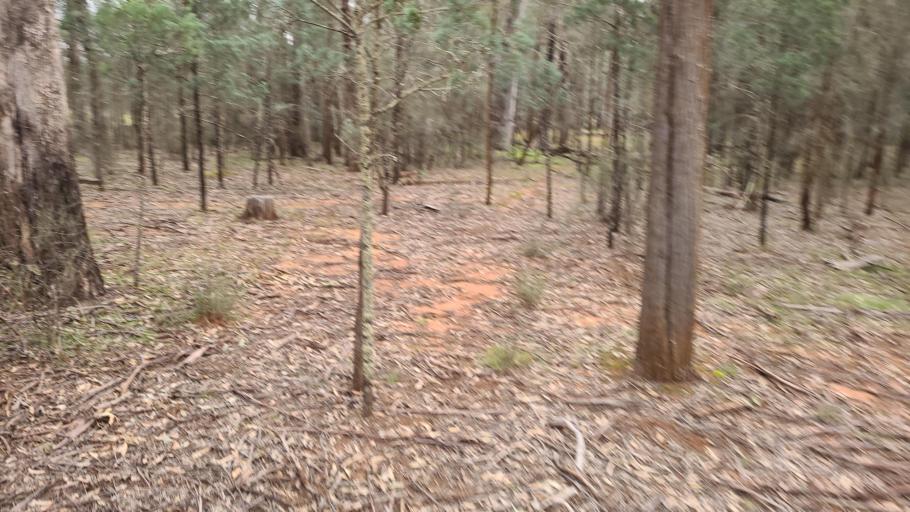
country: AU
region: New South Wales
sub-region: Coolamon
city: Coolamon
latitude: -34.8591
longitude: 146.9241
